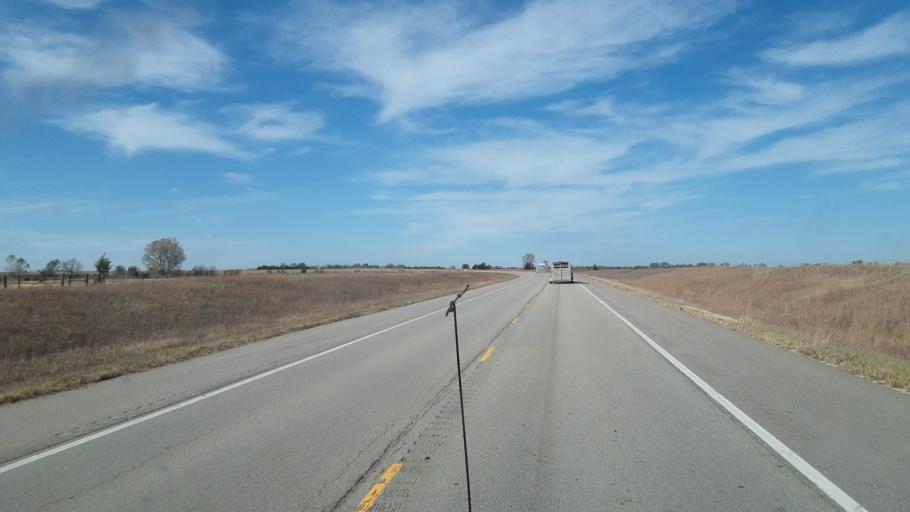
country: US
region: Kansas
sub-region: Marion County
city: Hillsboro
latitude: 38.3720
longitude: -97.3663
